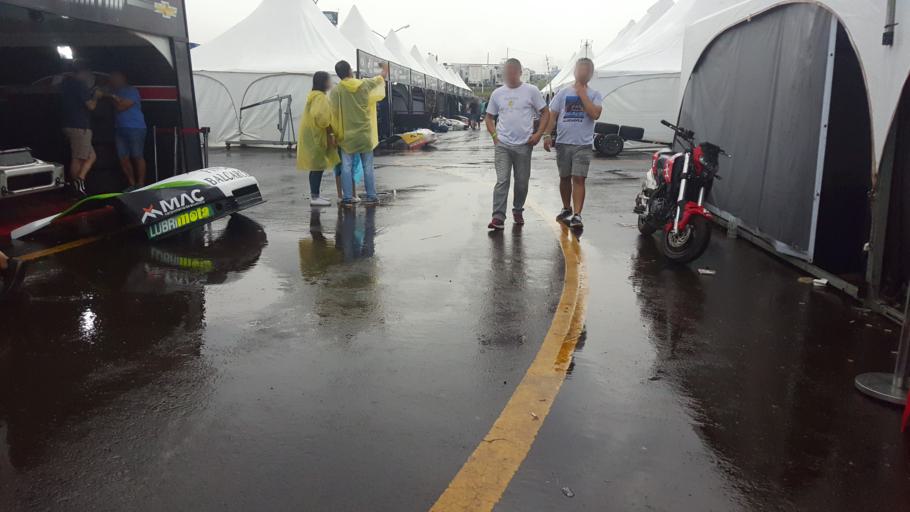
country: AR
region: Misiones
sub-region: Departamento de Capital
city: Posadas
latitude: -27.4394
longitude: -55.9264
